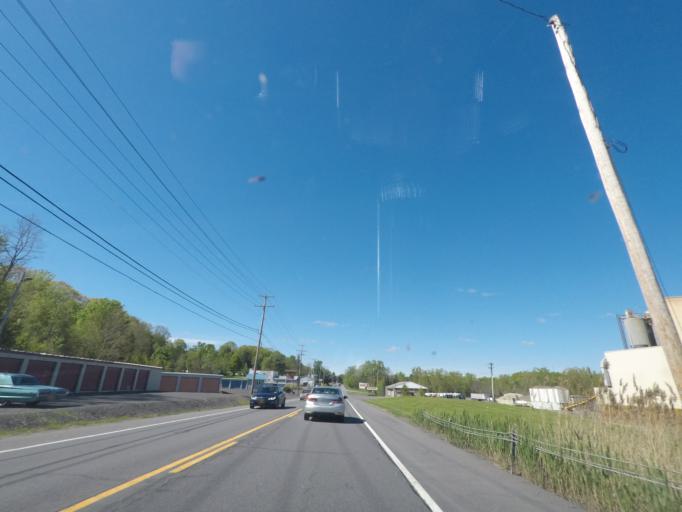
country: US
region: New York
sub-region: Albany County
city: Ravena
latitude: 42.4570
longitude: -73.8176
